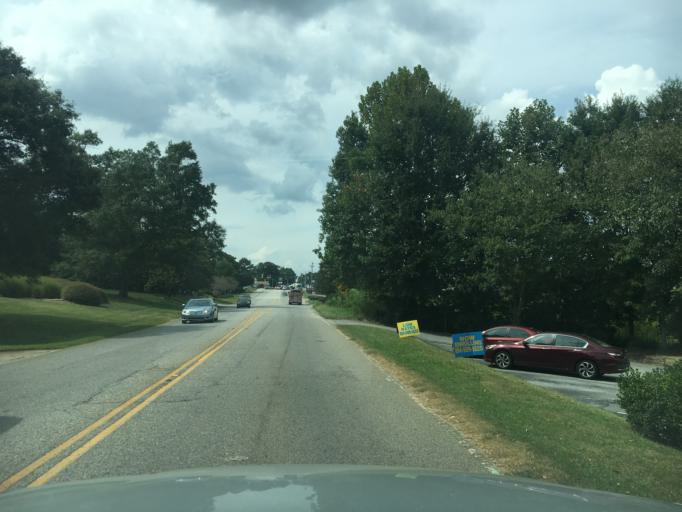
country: US
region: South Carolina
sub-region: Greenville County
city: Five Forks
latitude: 34.8494
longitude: -82.2277
